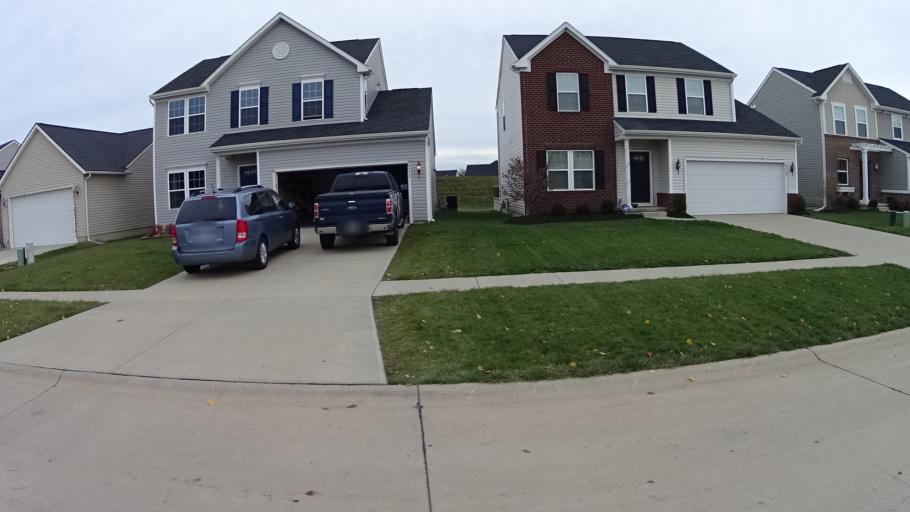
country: US
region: Ohio
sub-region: Lorain County
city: North Ridgeville
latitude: 41.3931
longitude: -82.0428
